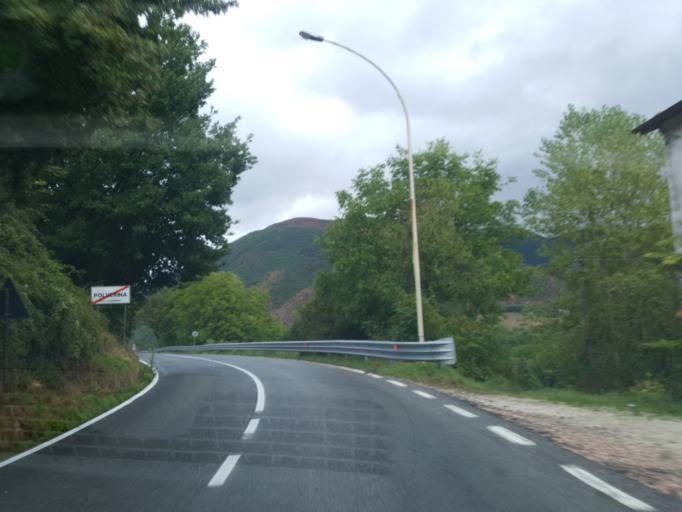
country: IT
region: The Marches
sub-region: Provincia di Macerata
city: Pievebovigliana
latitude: 43.0922
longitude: 13.1204
